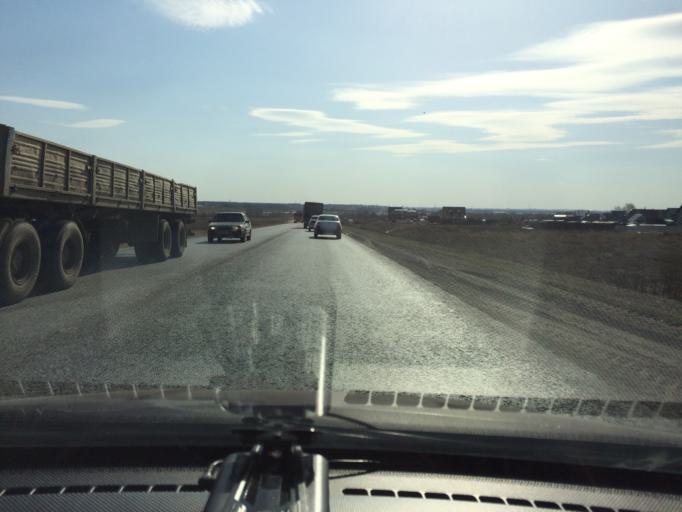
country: RU
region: Mariy-El
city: Yoshkar-Ola
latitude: 56.6942
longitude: 48.0566
